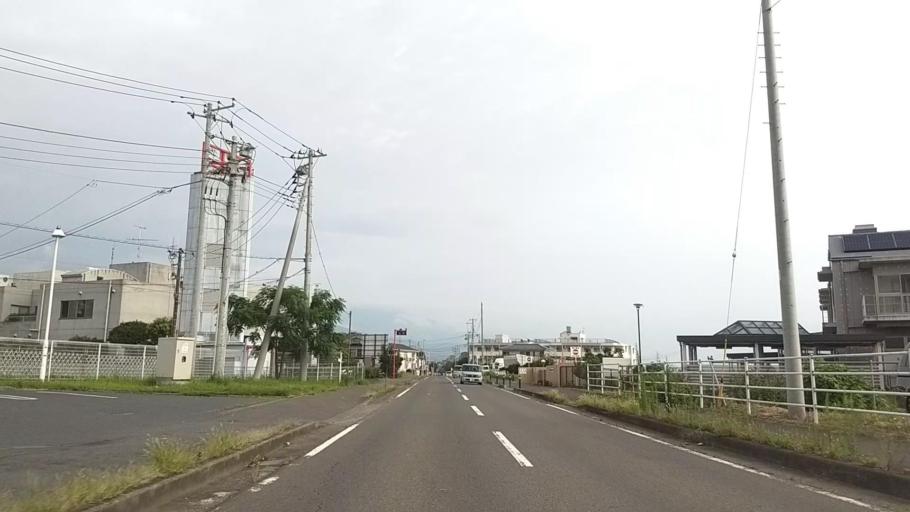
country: JP
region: Kanagawa
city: Oiso
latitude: 35.3446
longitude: 139.3059
